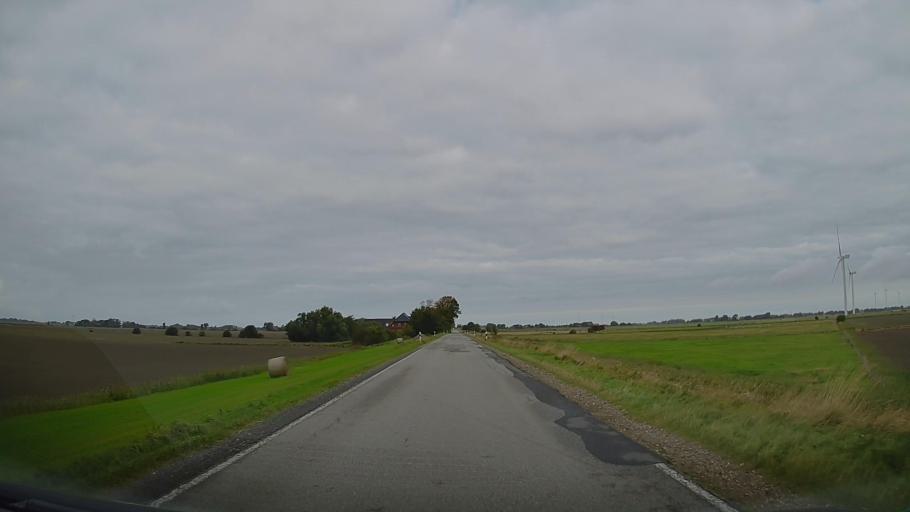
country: DE
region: Schleswig-Holstein
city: Emmelsbull-Horsbull
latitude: 54.7891
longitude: 8.7288
